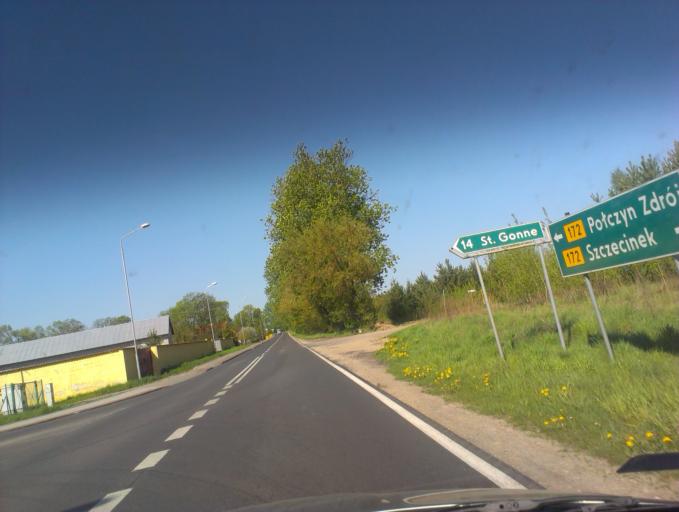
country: PL
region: West Pomeranian Voivodeship
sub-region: Powiat swidwinski
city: Polczyn-Zdroj
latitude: 53.7704
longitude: 16.1369
